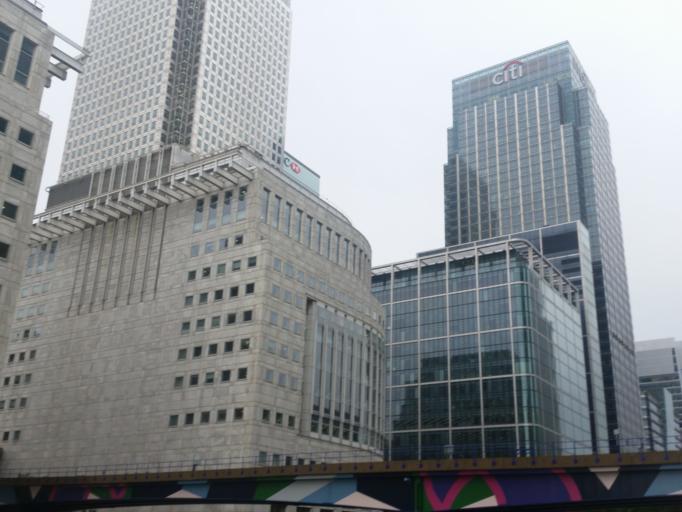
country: GB
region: England
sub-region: Greater London
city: Poplar
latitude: 51.5035
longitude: -0.0218
